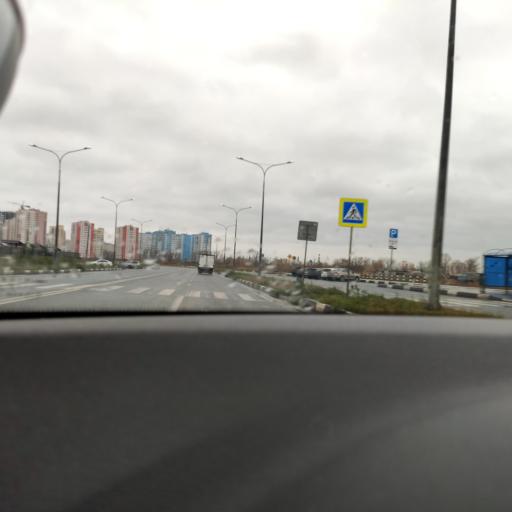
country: RU
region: Samara
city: Samara
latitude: 53.1394
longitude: 50.0781
